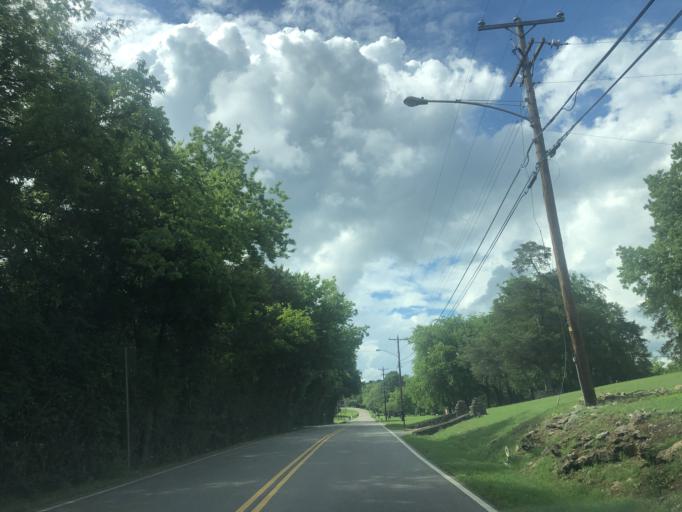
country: US
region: Tennessee
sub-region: Davidson County
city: Nashville
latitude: 36.2151
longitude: -86.8674
